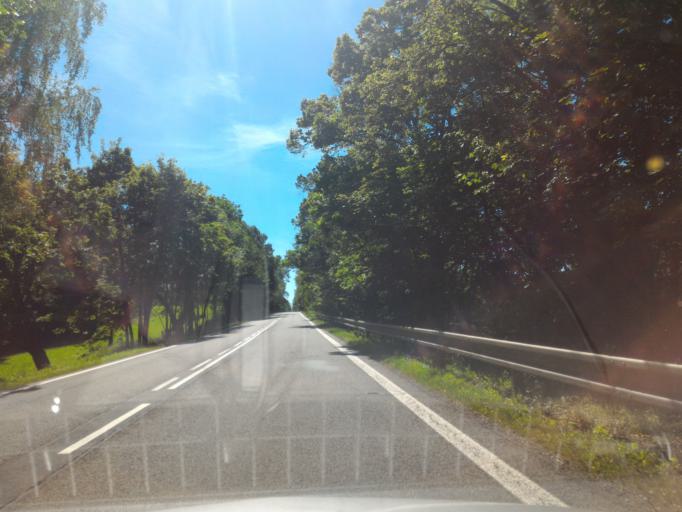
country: CZ
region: Vysocina
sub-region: Okres Jihlava
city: Jihlava
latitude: 49.3858
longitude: 15.5284
